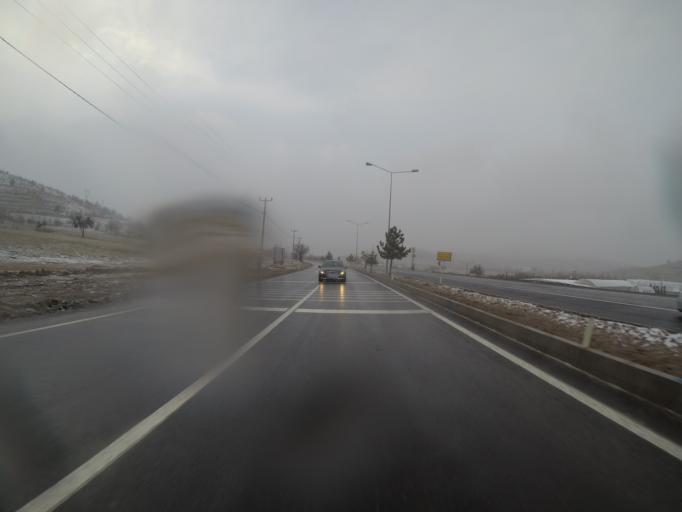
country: TR
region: Nevsehir
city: Nevsehir
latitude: 38.6305
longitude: 34.7633
